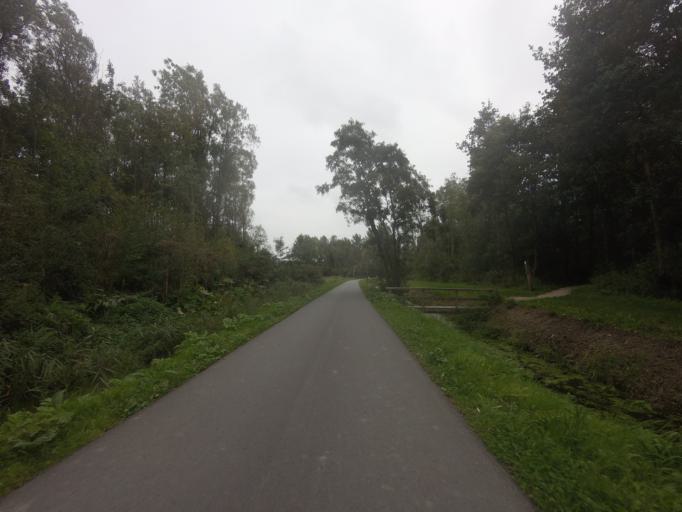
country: NL
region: Friesland
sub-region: Gemeente Leeuwarden
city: Bilgaard
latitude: 53.2215
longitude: 5.7898
